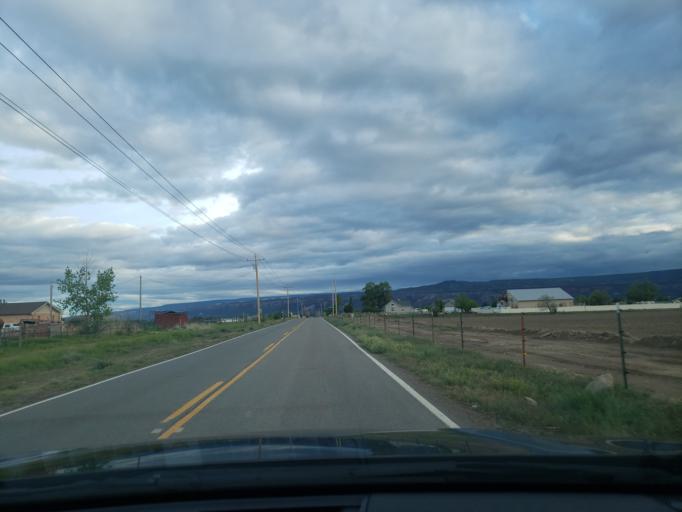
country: US
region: Colorado
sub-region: Mesa County
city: Fruita
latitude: 39.1948
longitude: -108.7012
